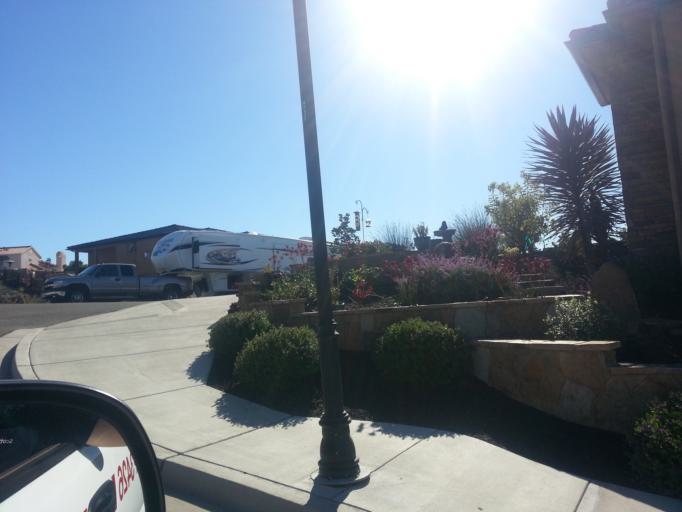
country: US
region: California
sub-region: San Luis Obispo County
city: Pismo Beach
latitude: 35.1451
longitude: -120.6257
